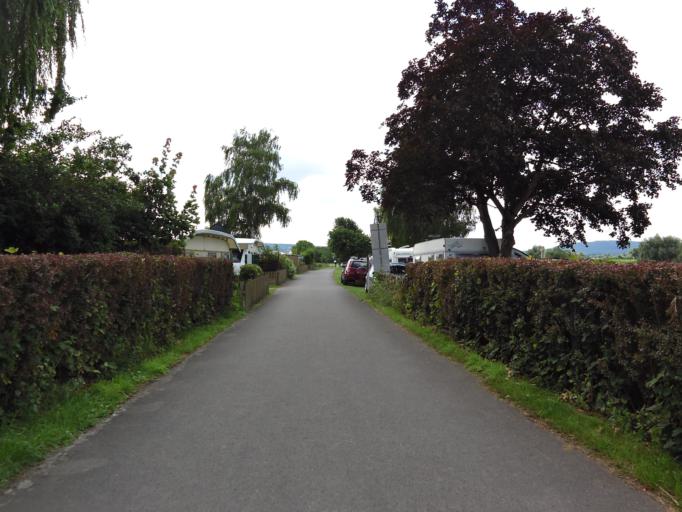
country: DE
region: North Rhine-Westphalia
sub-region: Regierungsbezirk Detmold
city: Hoexter
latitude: 51.7661
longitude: 9.3822
